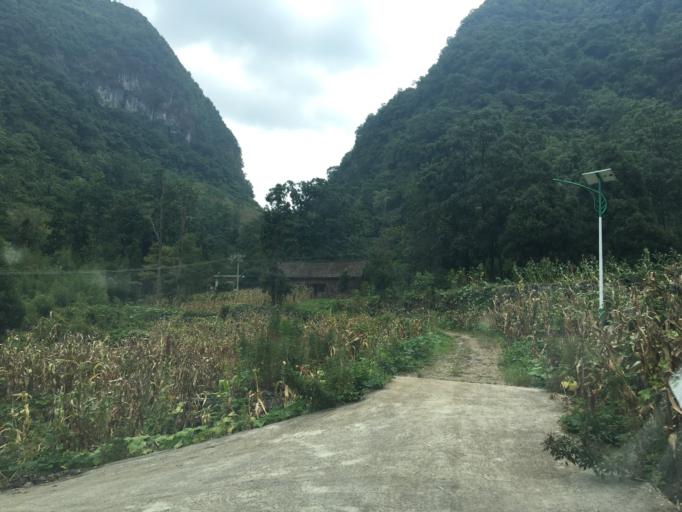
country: CN
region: Guangxi Zhuangzu Zizhiqu
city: Xinzhou
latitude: 25.2258
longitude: 105.6349
